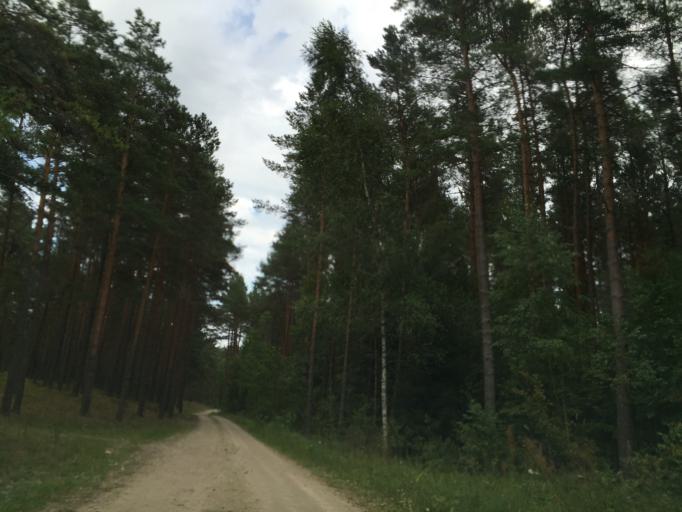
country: LV
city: Tireli
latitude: 56.8661
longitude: 23.6677
